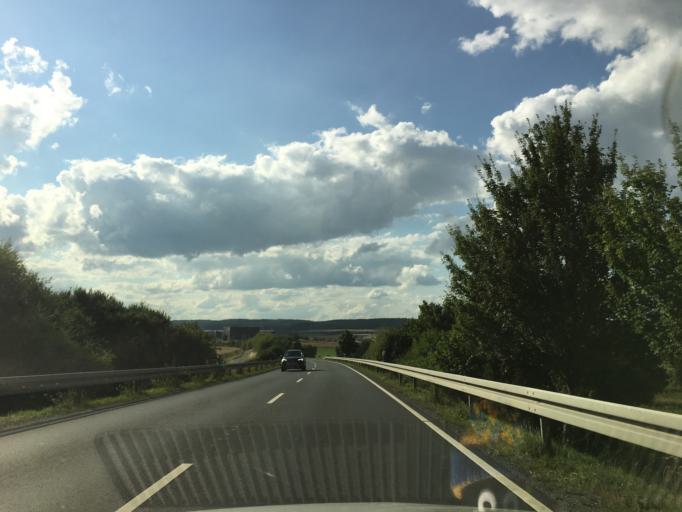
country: DE
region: Hesse
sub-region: Regierungsbezirk Darmstadt
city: Neu-Anspach
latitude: 50.3033
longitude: 8.5290
